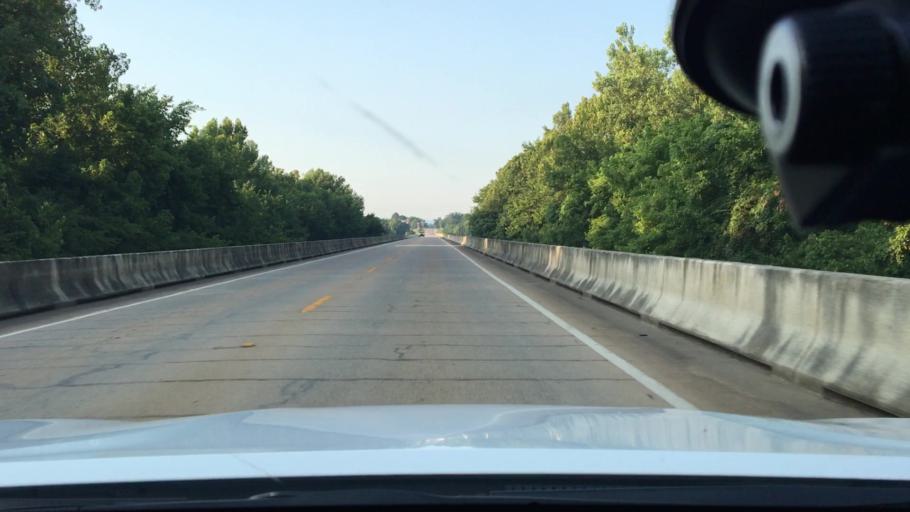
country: US
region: Arkansas
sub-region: Johnson County
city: Clarksville
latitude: 35.3983
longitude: -93.5309
